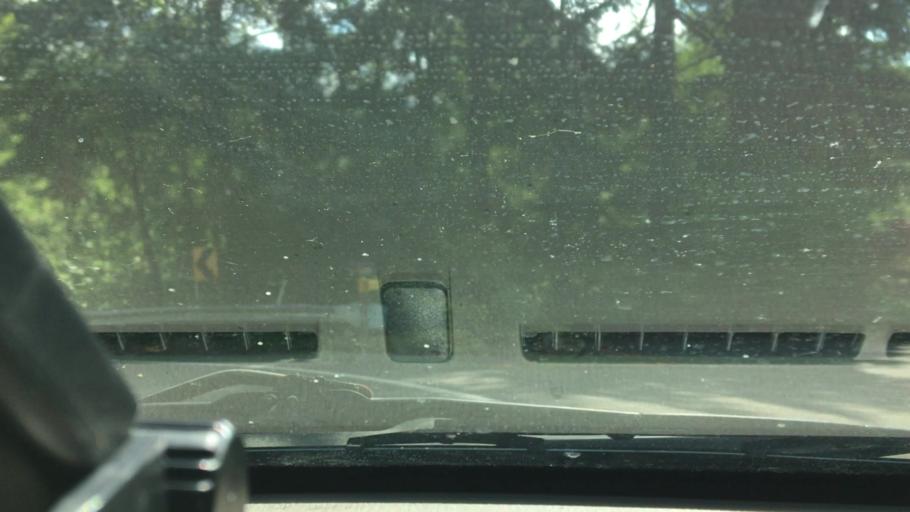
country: US
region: Washington
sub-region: Whatcom County
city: Geneva
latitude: 48.7608
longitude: -122.3668
